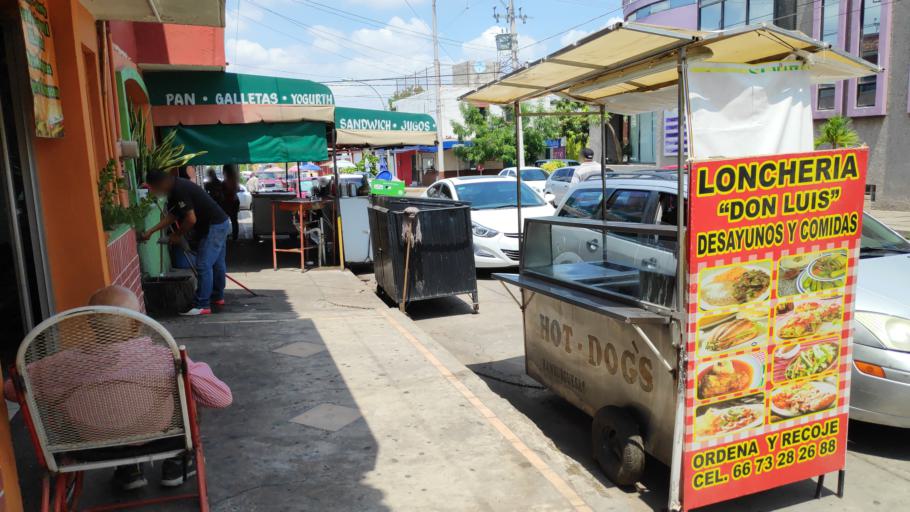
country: MX
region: Sinaloa
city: Culiacan
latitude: 24.8072
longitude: -107.3851
